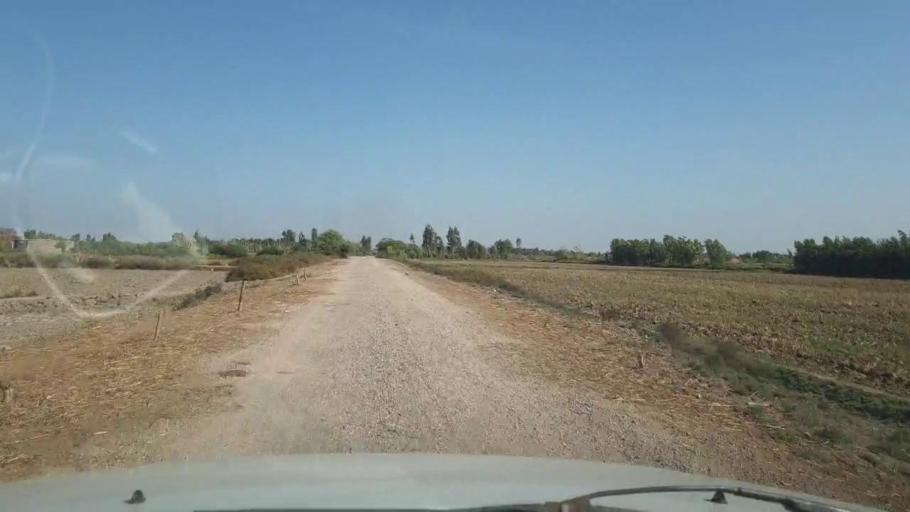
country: PK
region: Sindh
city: Mirpur Sakro
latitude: 24.4867
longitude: 67.8104
